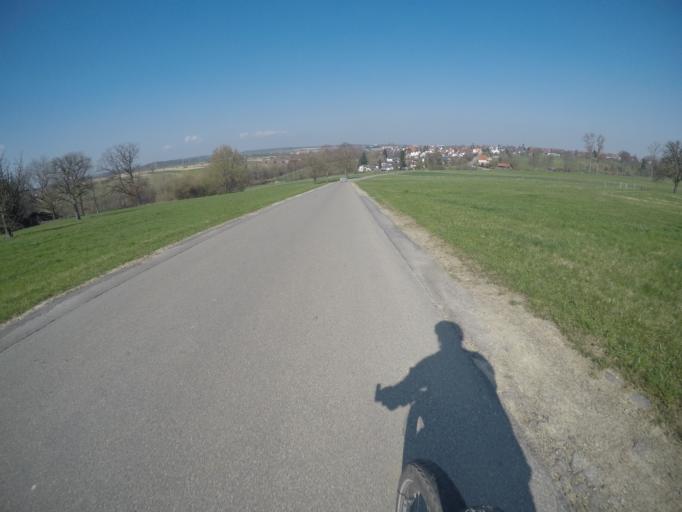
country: DE
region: Baden-Wuerttemberg
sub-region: Tuebingen Region
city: Pliezhausen
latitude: 48.5683
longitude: 9.1806
